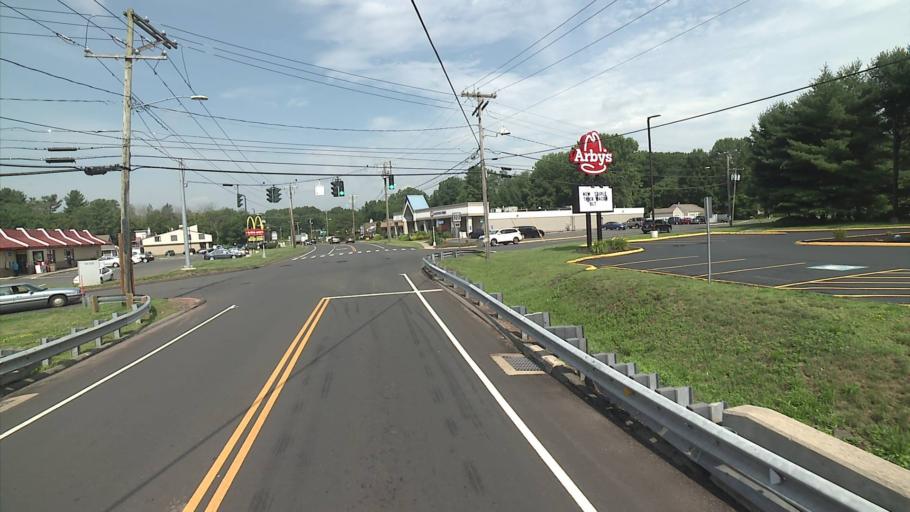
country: US
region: Connecticut
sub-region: New Haven County
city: Cheshire Village
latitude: 41.5630
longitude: -72.8736
